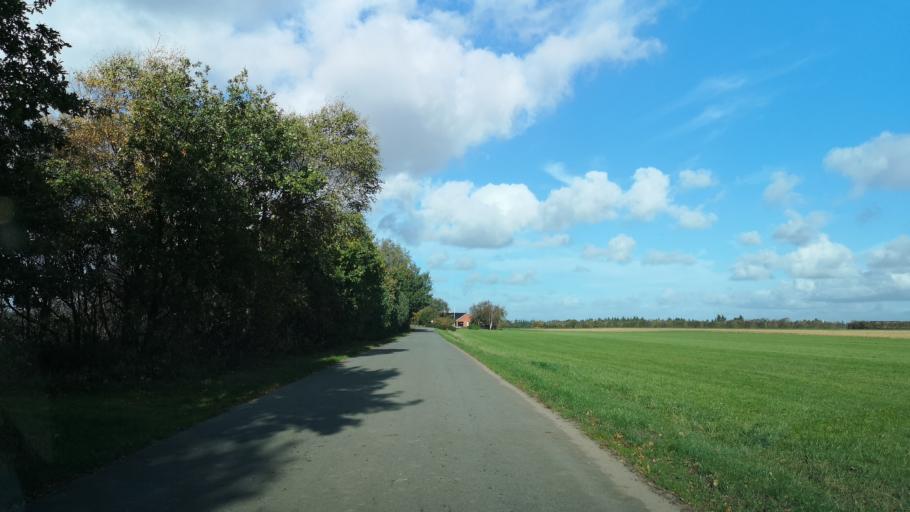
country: DK
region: South Denmark
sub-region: Varde Kommune
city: Oksbol
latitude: 55.7067
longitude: 8.2761
